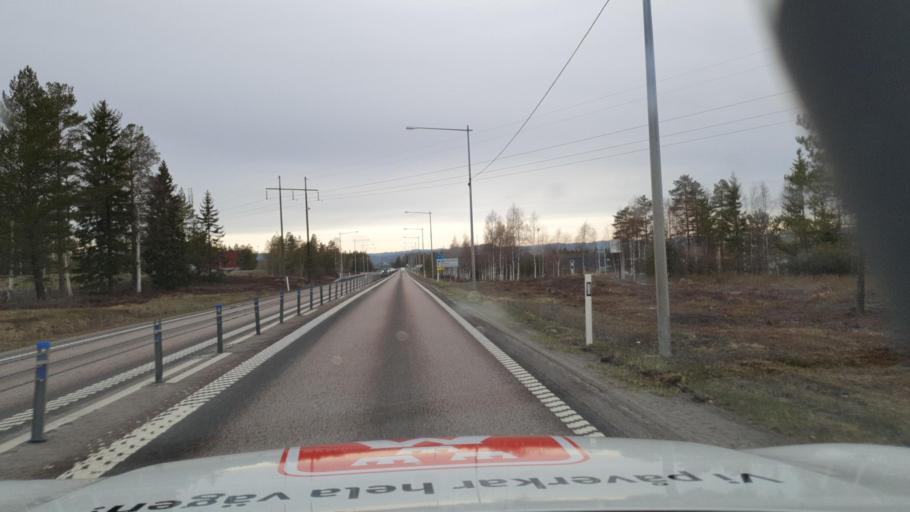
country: SE
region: Vaesternorrland
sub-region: Haernoesands Kommun
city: Haernoesand
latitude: 62.6510
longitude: 17.8928
